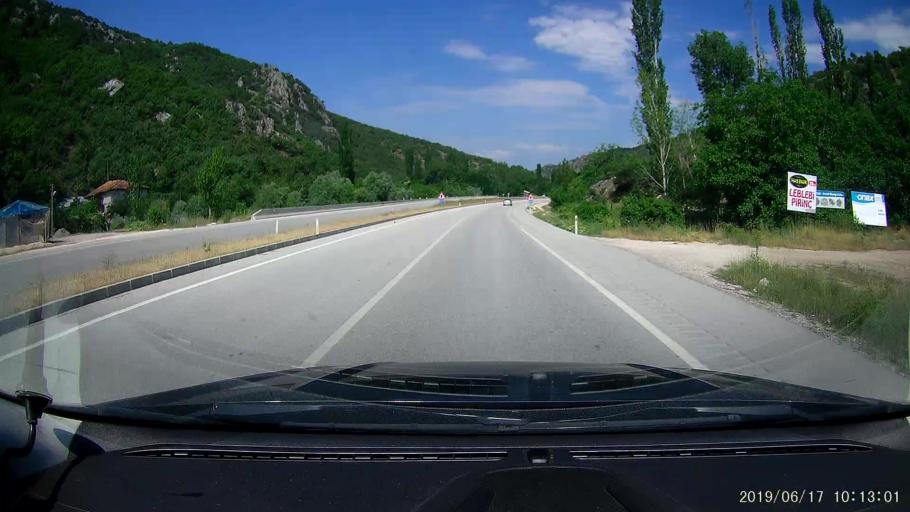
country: TR
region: Amasya
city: Saraycik
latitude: 40.9833
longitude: 35.0573
